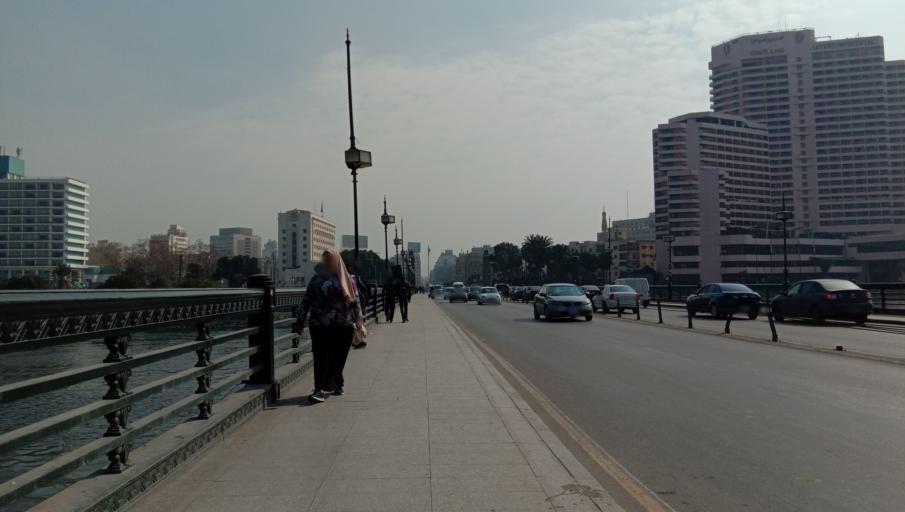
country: EG
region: Muhafazat al Qahirah
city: Cairo
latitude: 30.0438
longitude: 31.2293
